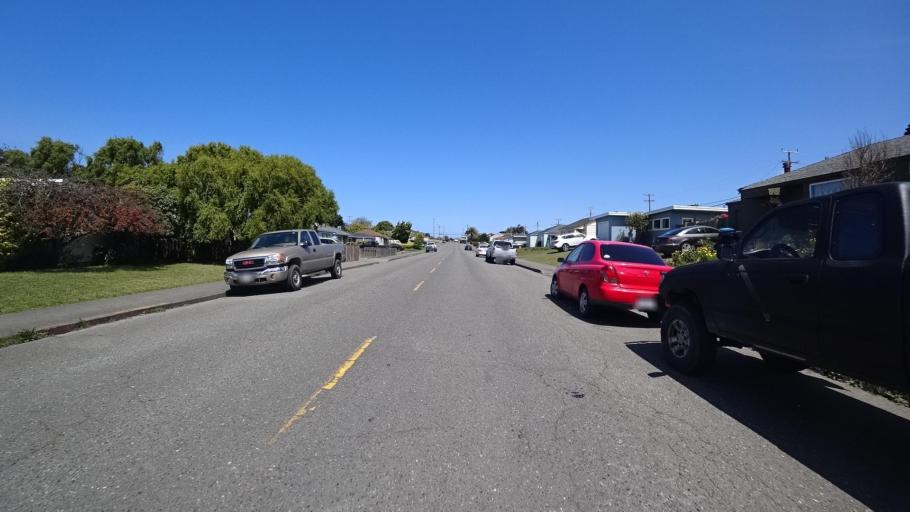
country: US
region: California
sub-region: Humboldt County
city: Bayview
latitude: 40.7781
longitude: -124.1835
